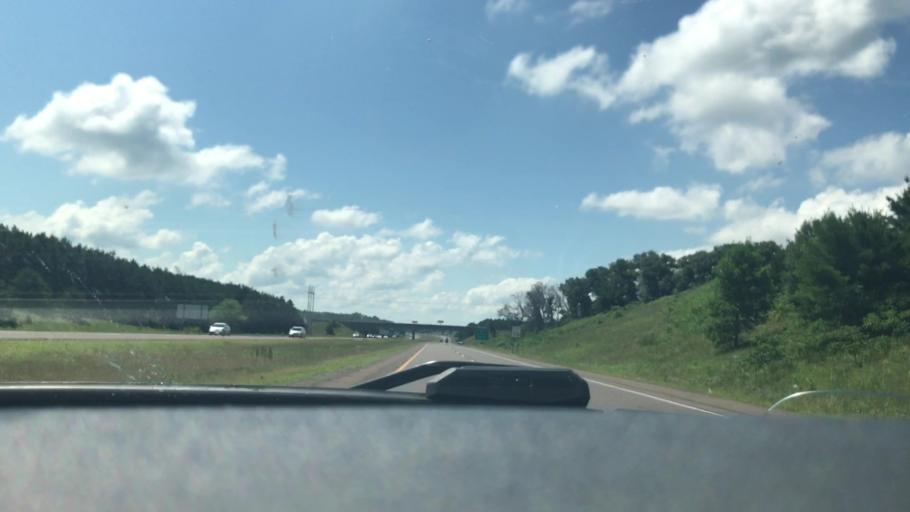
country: US
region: Wisconsin
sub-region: Chippewa County
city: Chippewa Falls
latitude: 44.9186
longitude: -91.4282
